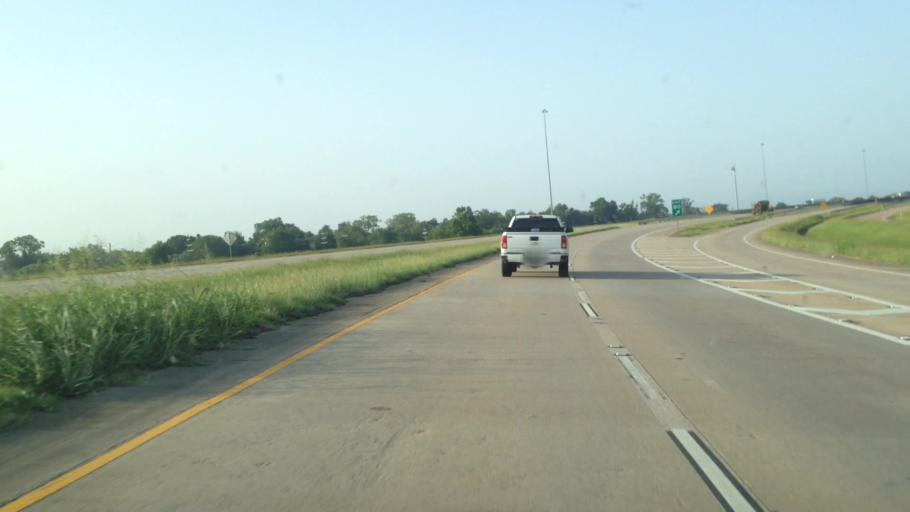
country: US
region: Louisiana
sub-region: Rapides Parish
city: Alexandria
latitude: 31.2475
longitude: -92.4290
